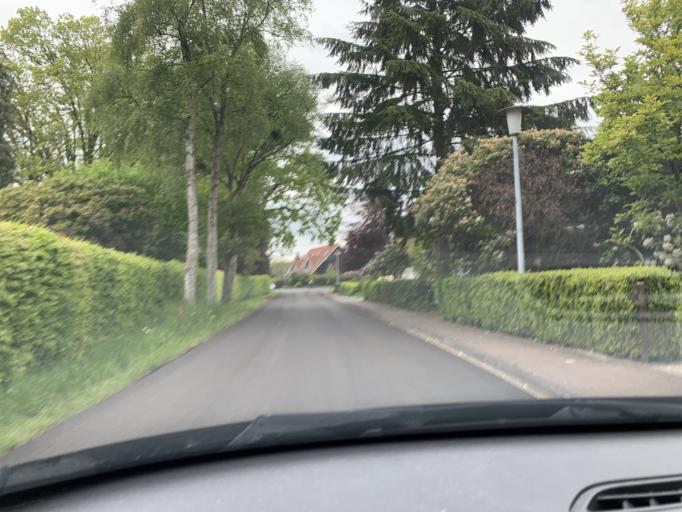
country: DE
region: Lower Saxony
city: Westerstede
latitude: 53.2483
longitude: 7.9129
